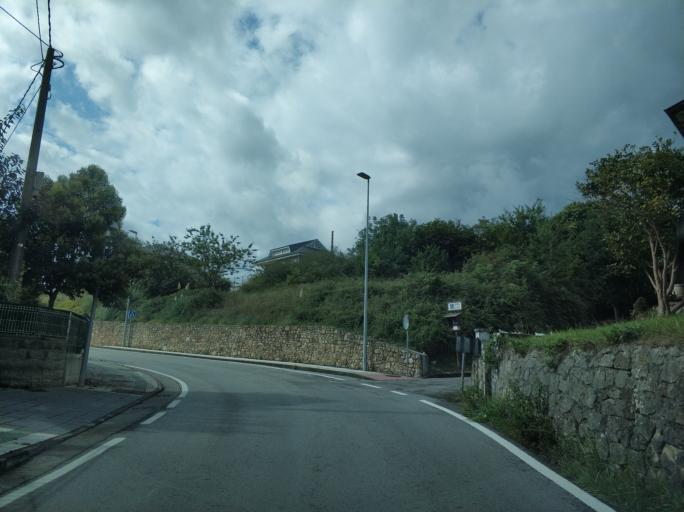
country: ES
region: Cantabria
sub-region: Provincia de Cantabria
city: Miengo
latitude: 43.4008
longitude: -3.9512
